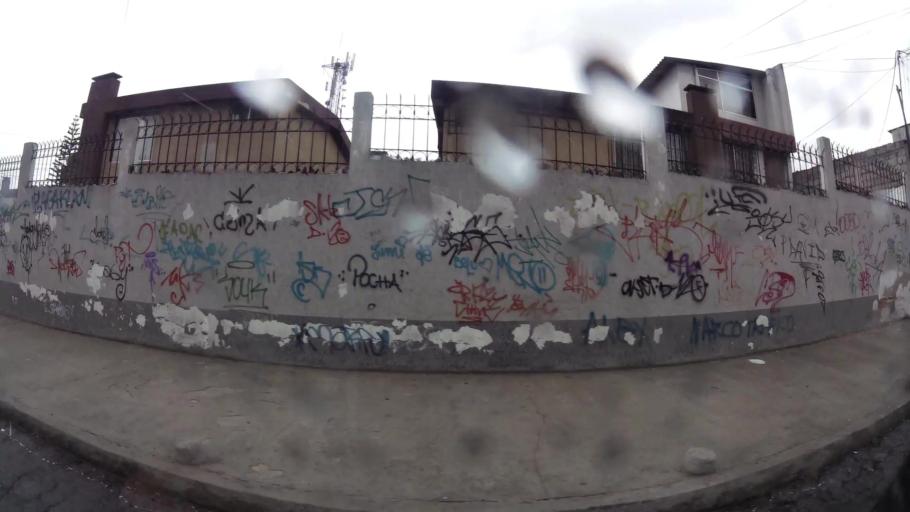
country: EC
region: Pichincha
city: Quito
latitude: -0.1223
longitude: -78.4946
